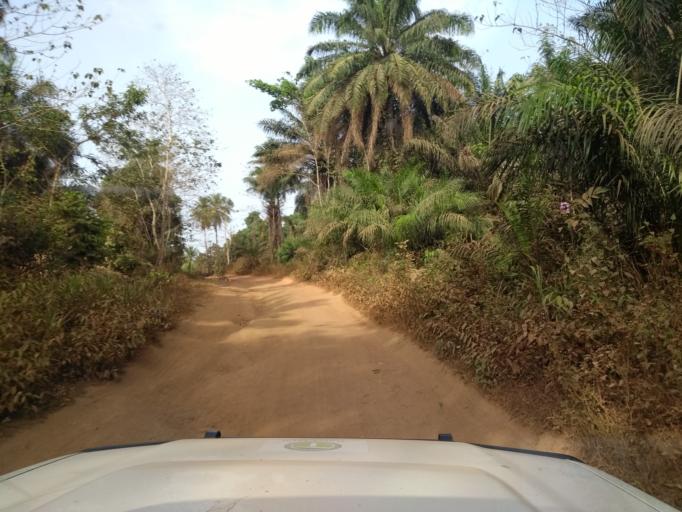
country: GN
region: Kindia
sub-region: Prefecture de Dubreka
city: Dubreka
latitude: 9.8625
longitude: -13.5453
